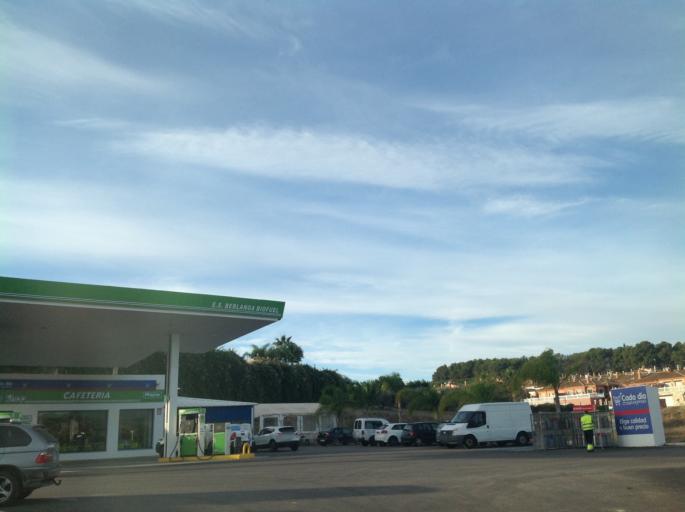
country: ES
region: Andalusia
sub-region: Provincia de Malaga
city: Pizarra
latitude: 36.7481
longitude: -4.7159
